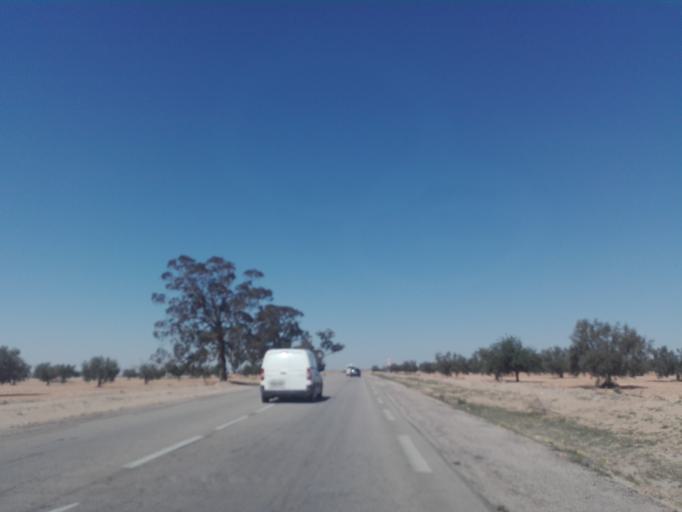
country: TN
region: Safaqis
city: Bi'r `Ali Bin Khalifah
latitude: 34.7587
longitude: 10.3050
